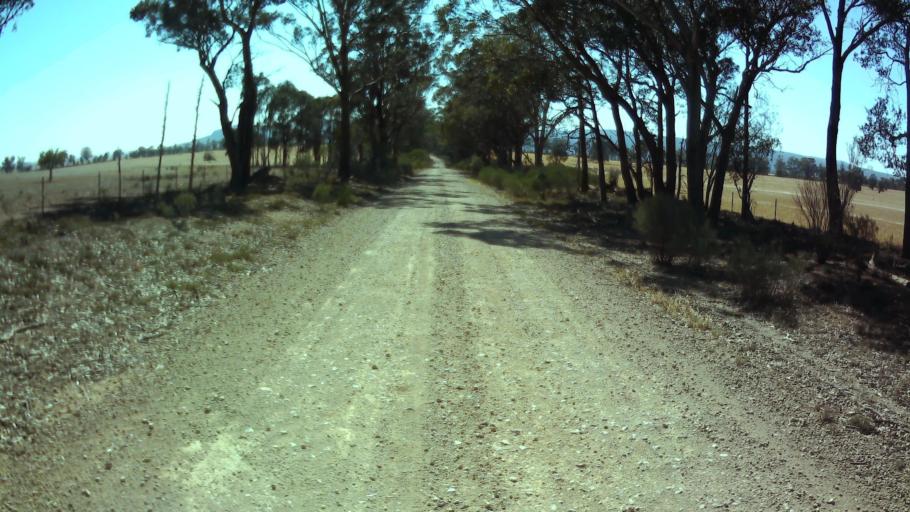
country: AU
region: New South Wales
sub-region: Weddin
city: Grenfell
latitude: -33.9016
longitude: 147.8690
